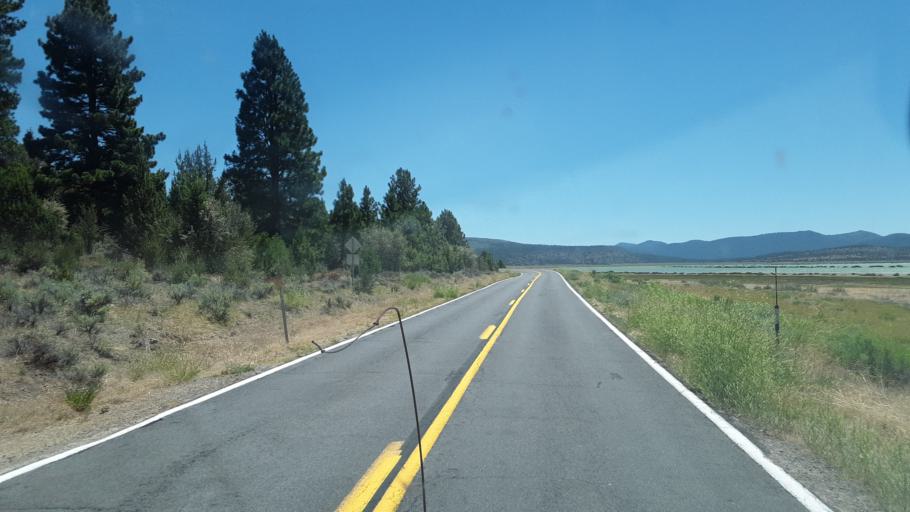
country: US
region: California
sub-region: Lassen County
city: Susanville
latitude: 40.6870
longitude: -120.6627
